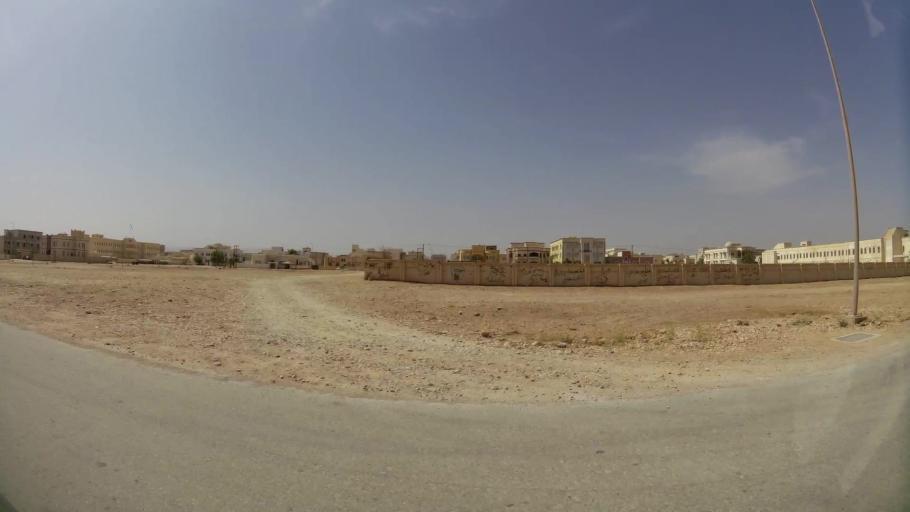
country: OM
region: Zufar
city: Salalah
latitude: 17.0433
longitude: 54.1525
